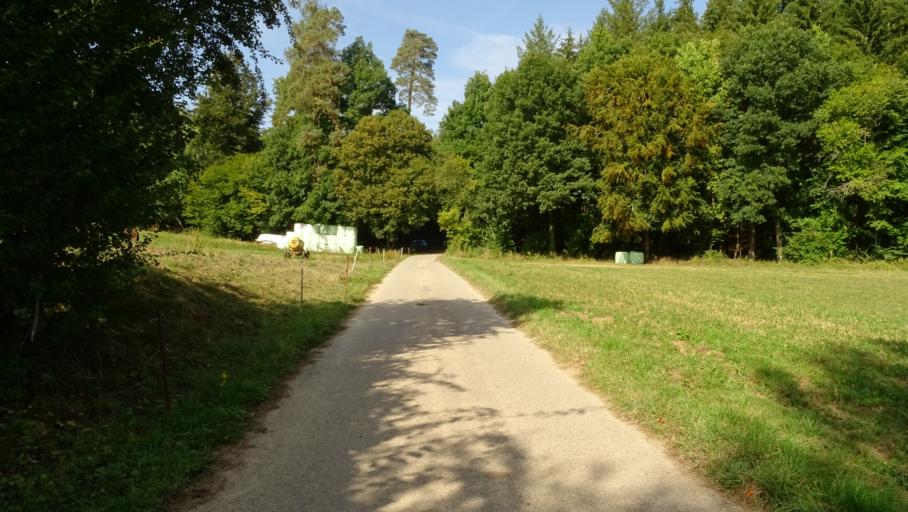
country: DE
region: Baden-Wuerttemberg
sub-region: Karlsruhe Region
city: Mosbach
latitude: 49.3874
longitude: 9.1644
